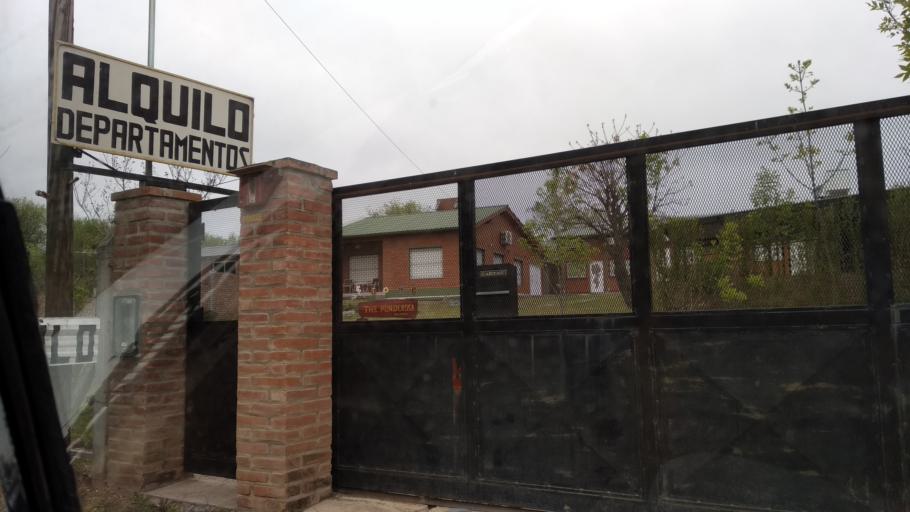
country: AR
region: Cordoba
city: Mina Clavero
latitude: -31.7148
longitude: -65.0052
